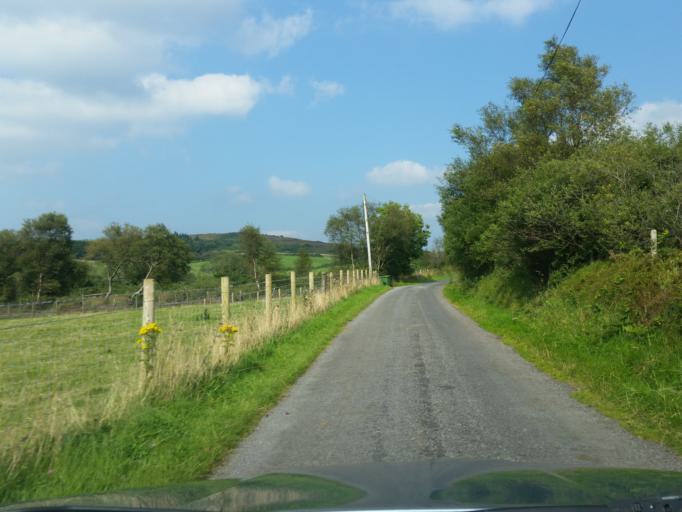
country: GB
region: Northern Ireland
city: Ballinamallard
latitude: 54.3422
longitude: -7.5260
